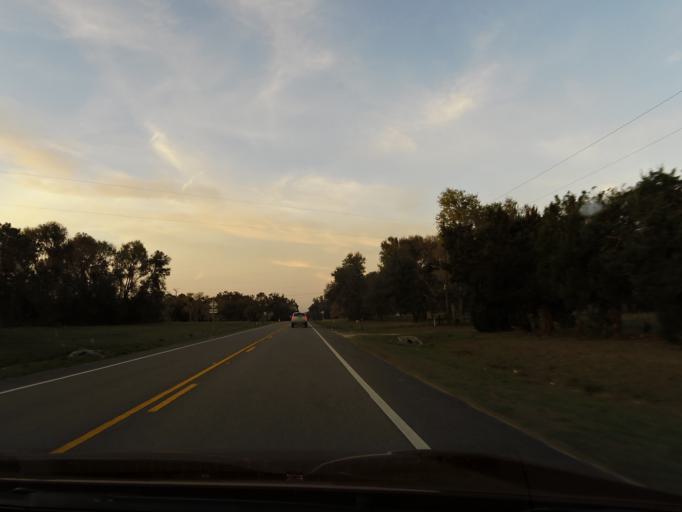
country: US
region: Florida
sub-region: Volusia County
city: De Leon Springs
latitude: 29.1293
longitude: -81.2853
